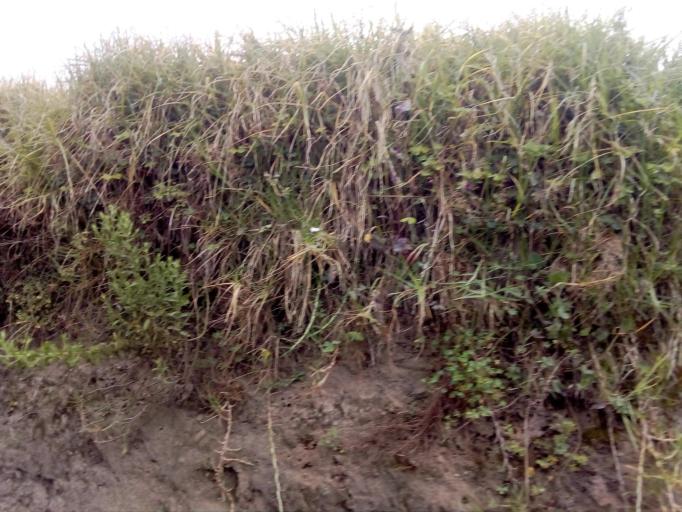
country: GT
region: Quetzaltenango
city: Olintepeque
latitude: 14.8612
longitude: -91.5018
